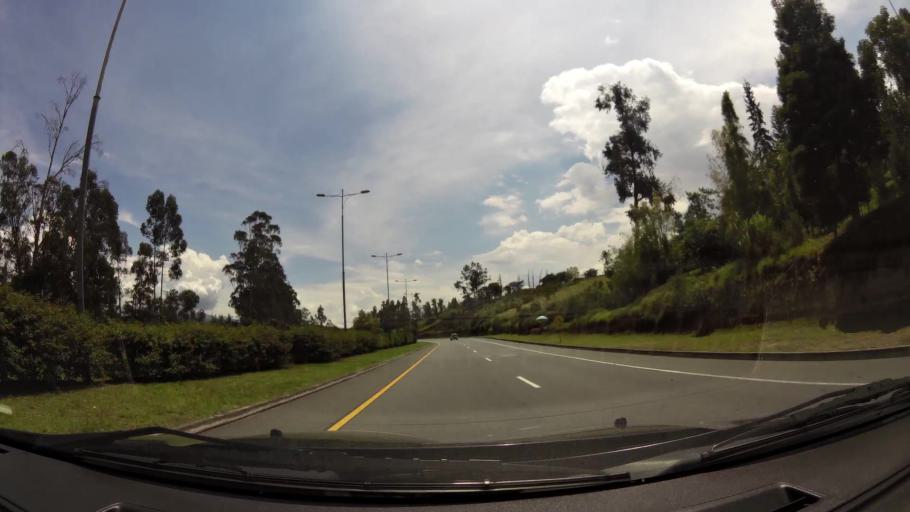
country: EC
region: Pichincha
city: Sangolqui
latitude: -0.1838
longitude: -78.3395
